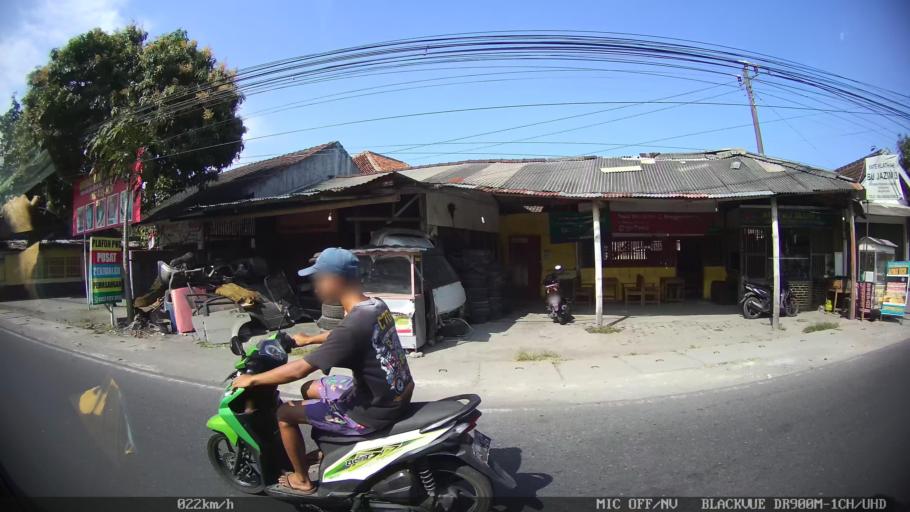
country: ID
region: Daerah Istimewa Yogyakarta
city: Sewon
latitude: -7.8652
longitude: 110.3898
